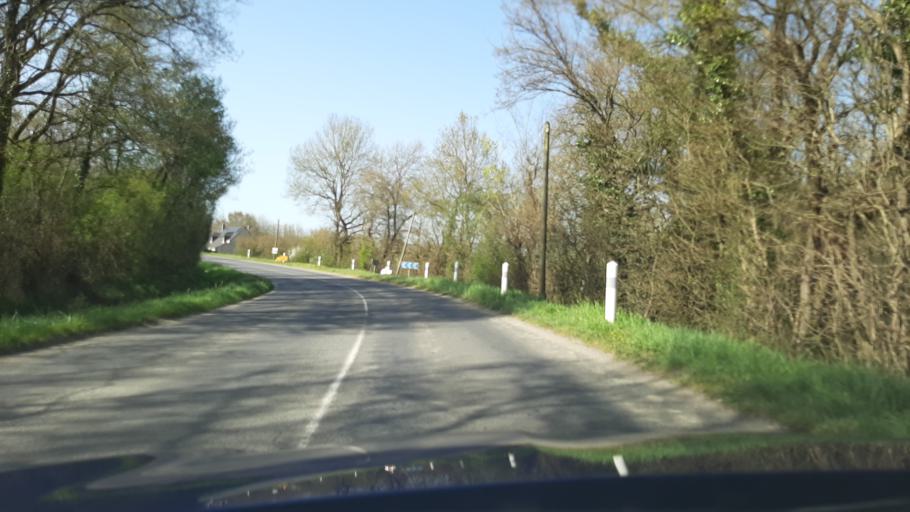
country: FR
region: Pays de la Loire
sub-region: Departement de Maine-et-Loire
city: Les Ponts-de-Ce
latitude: 47.4024
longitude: -0.5169
